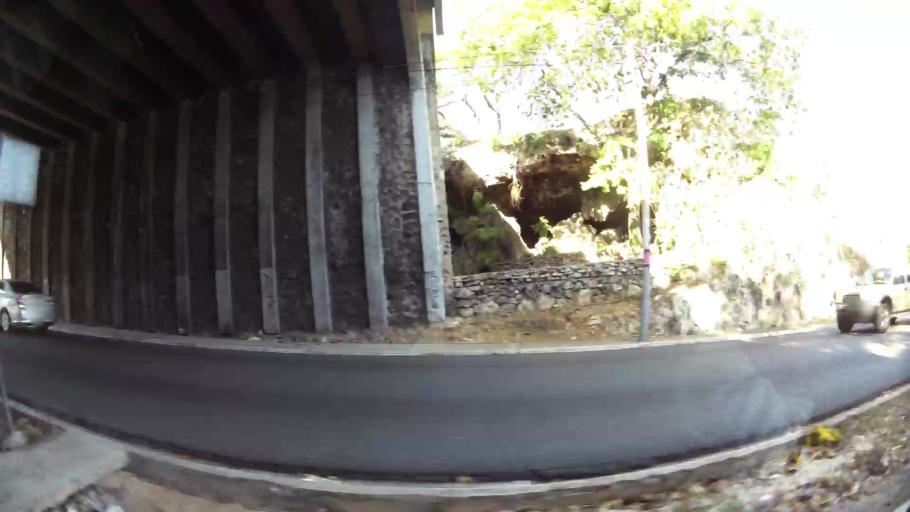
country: DO
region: Nacional
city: Bella Vista
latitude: 18.4505
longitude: -69.9365
